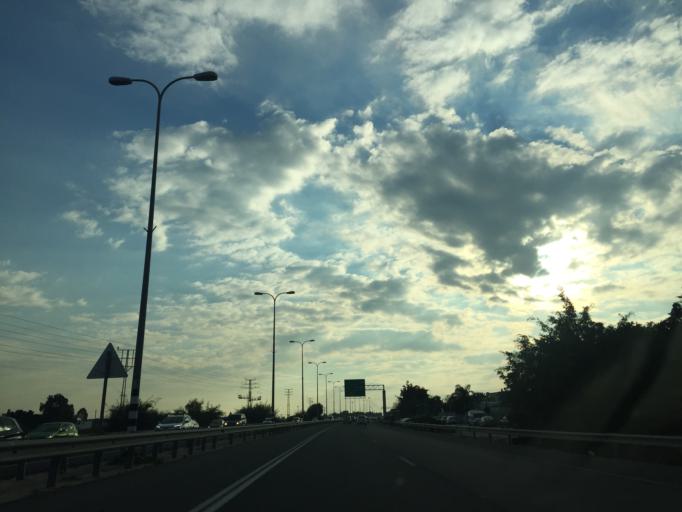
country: IL
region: Central District
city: Lod
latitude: 31.9310
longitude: 34.8902
